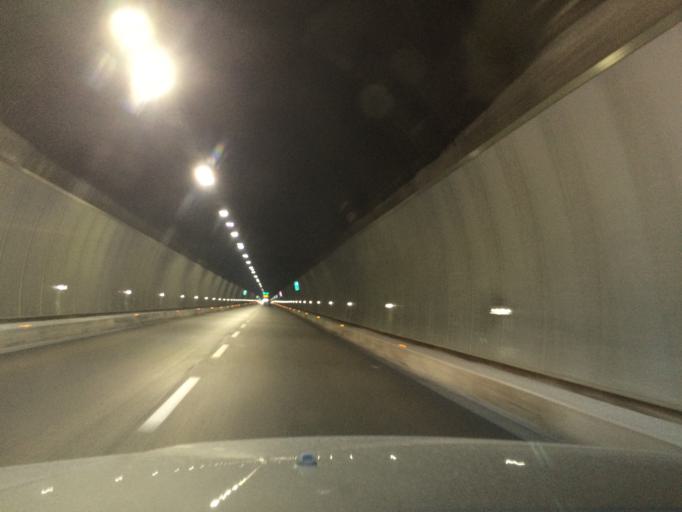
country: IT
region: Umbria
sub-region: Provincia di Perugia
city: Massa Martana
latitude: 42.7467
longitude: 12.4709
